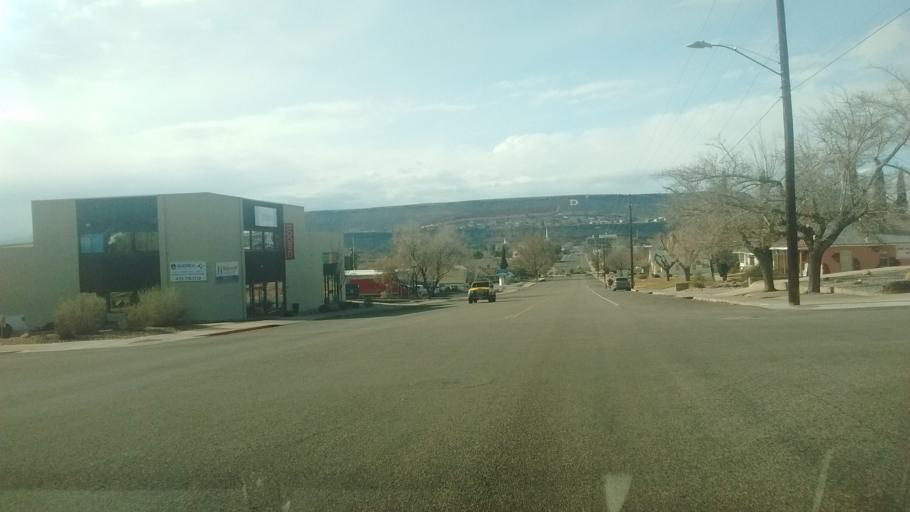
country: US
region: Utah
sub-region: Washington County
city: Saint George
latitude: 37.1082
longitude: -113.5704
